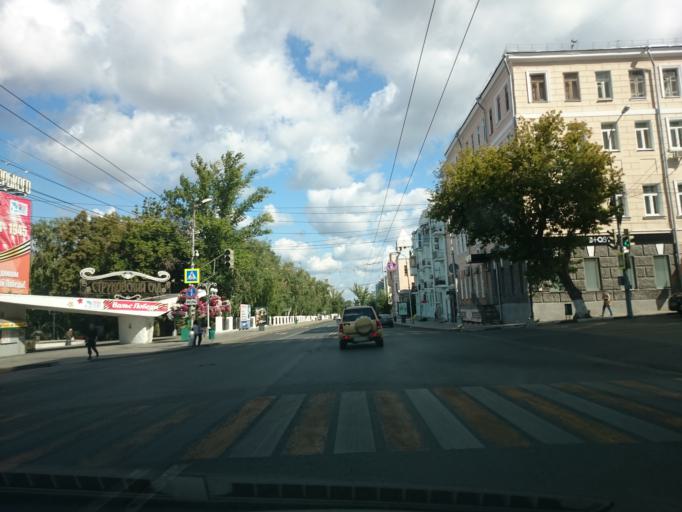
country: RU
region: Samara
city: Rozhdestveno
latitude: 53.1948
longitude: 50.0938
